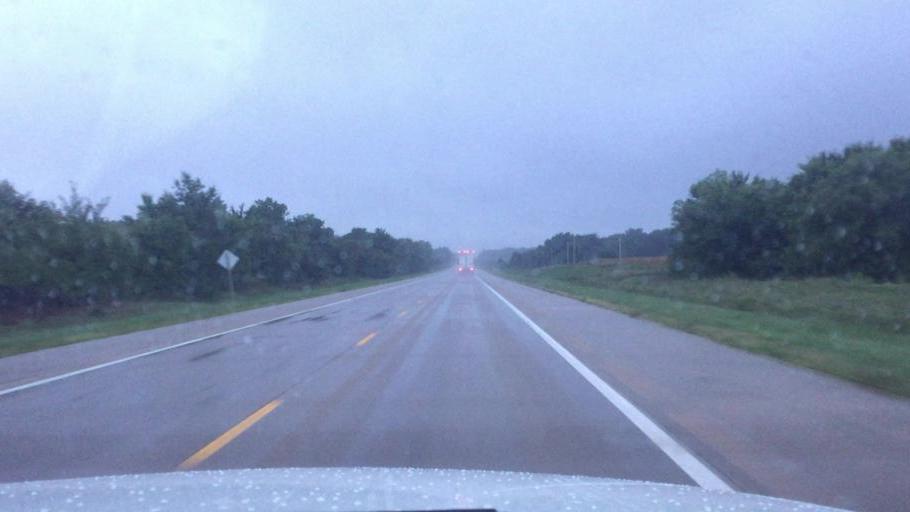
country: US
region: Kansas
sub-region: Neosho County
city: Chanute
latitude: 37.5606
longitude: -95.4709
